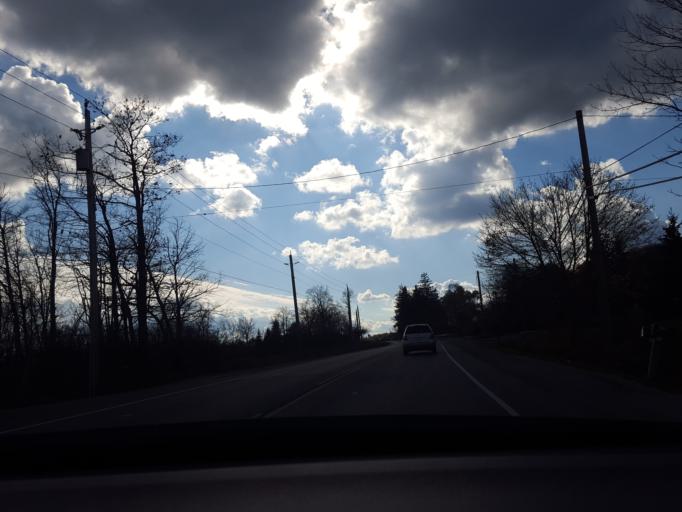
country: CA
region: Ontario
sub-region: Halton
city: Milton
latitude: 43.4722
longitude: -79.8995
